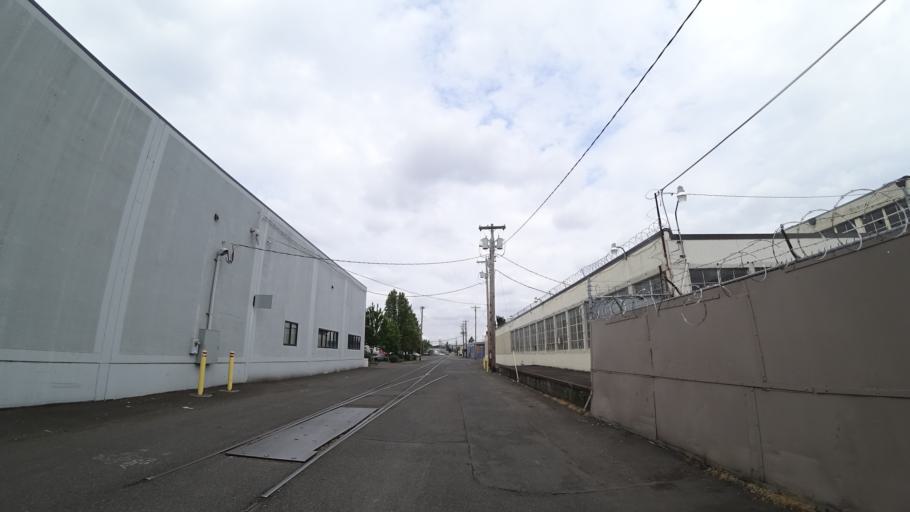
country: US
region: Oregon
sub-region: Clackamas County
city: Milwaukie
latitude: 45.4862
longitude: -122.6416
